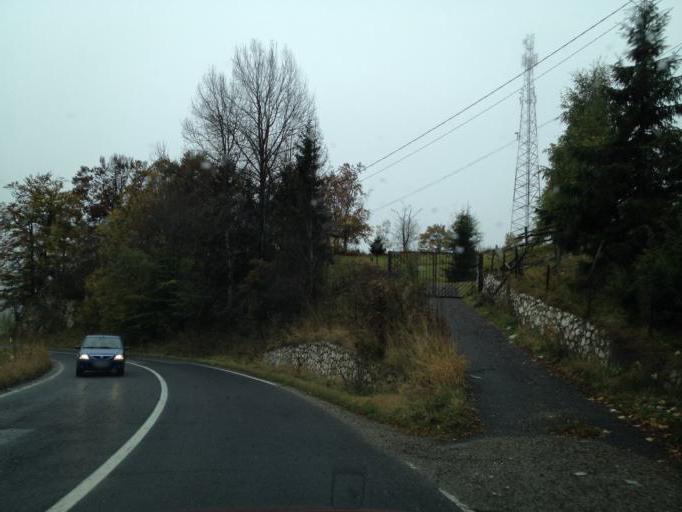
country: RO
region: Brasov
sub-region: Comuna Fundata
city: Fundata
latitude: 45.4447
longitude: 25.2780
